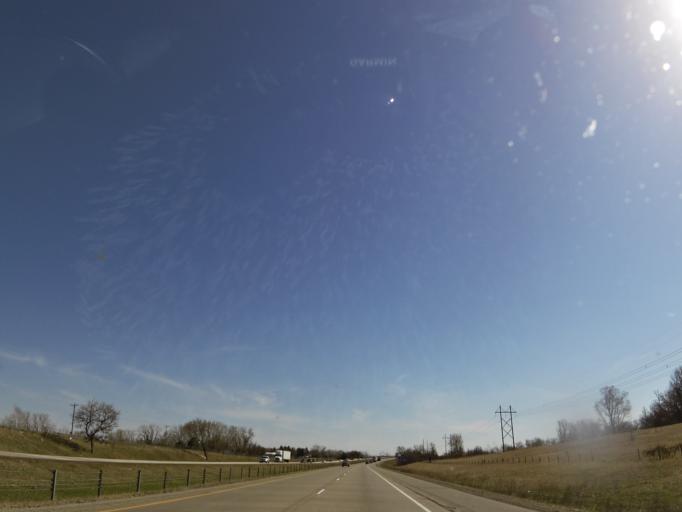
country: US
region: Minnesota
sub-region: Dakota County
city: Lakeville
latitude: 44.6618
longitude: -93.2942
